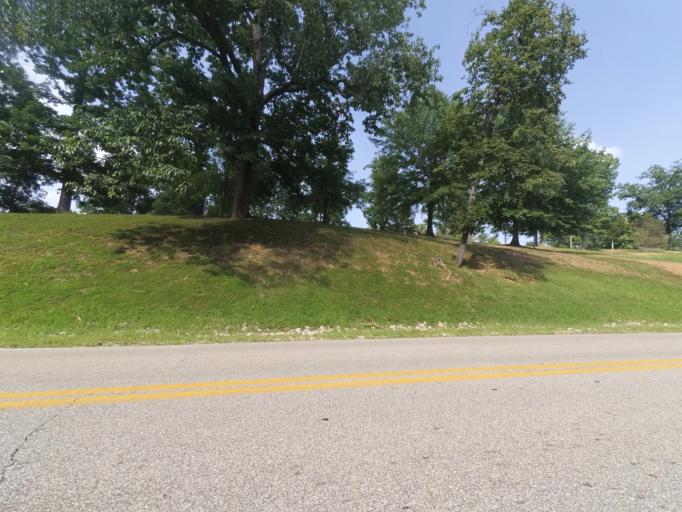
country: US
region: Ohio
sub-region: Lawrence County
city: Burlington
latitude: 38.3794
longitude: -82.5172
